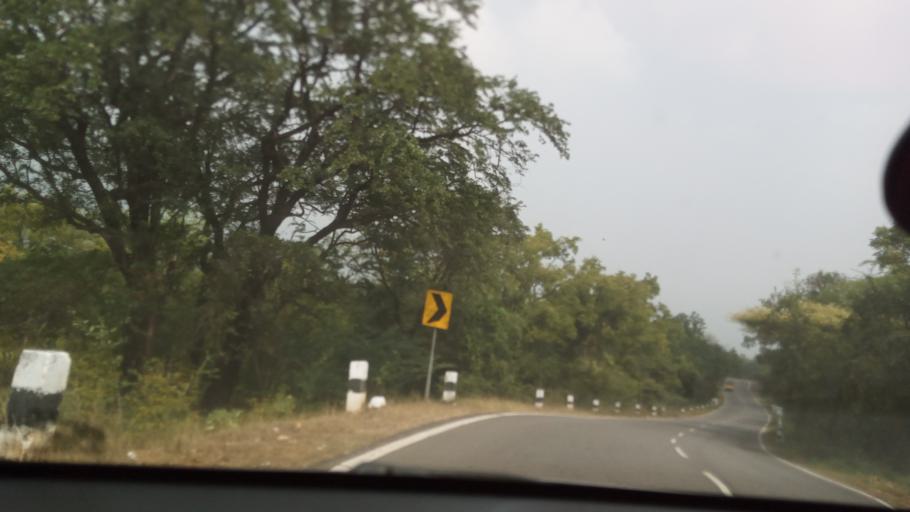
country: IN
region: Tamil Nadu
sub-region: Erode
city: Sathyamangalam
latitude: 11.5654
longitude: 77.1349
